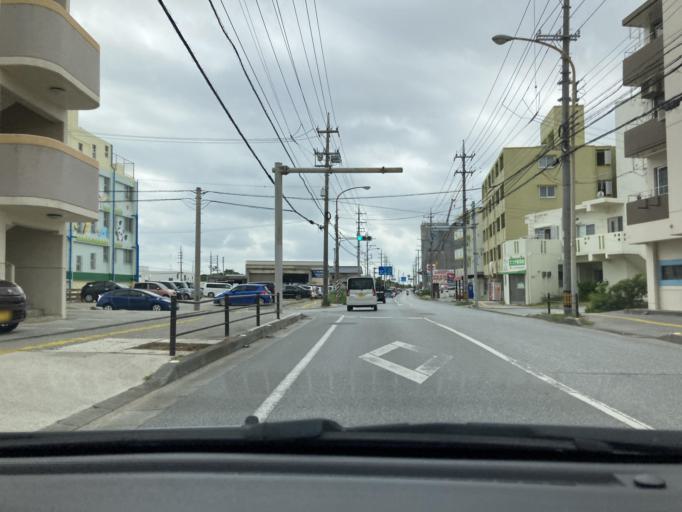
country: JP
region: Okinawa
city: Ginowan
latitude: 26.2439
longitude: 127.7681
